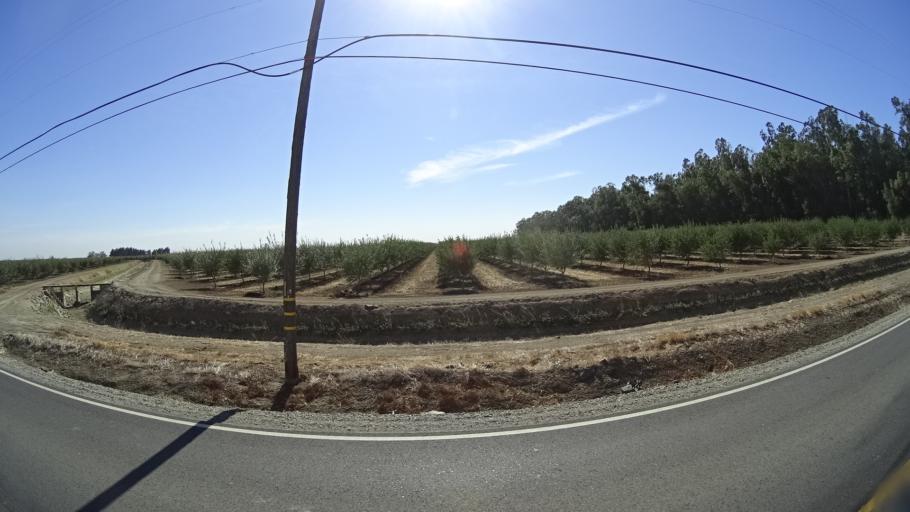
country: US
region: California
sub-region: Yolo County
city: Woodland
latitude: 38.6200
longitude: -121.8663
